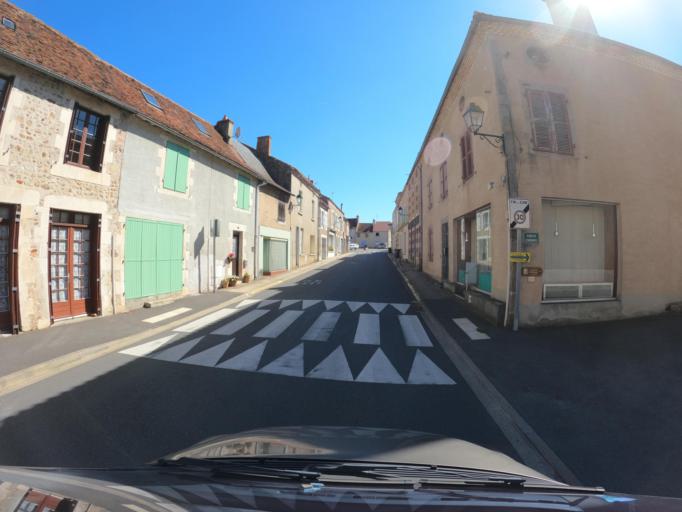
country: FR
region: Poitou-Charentes
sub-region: Departement de la Vienne
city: Lathus-Saint-Remy
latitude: 46.3333
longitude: 0.9592
